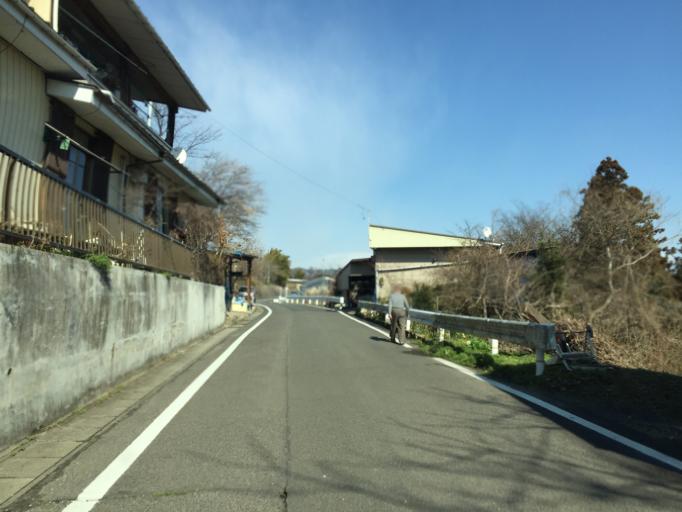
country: JP
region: Fukushima
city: Fukushima-shi
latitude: 37.8242
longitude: 140.4246
